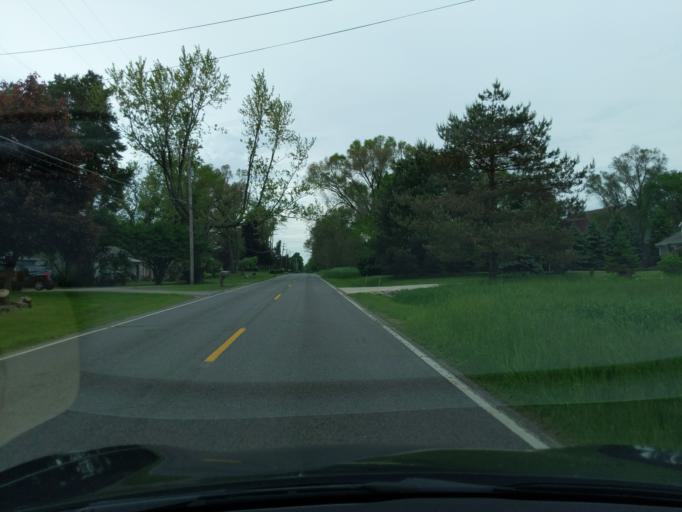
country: US
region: Michigan
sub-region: Ingham County
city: Leslie
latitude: 42.3745
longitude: -84.3492
